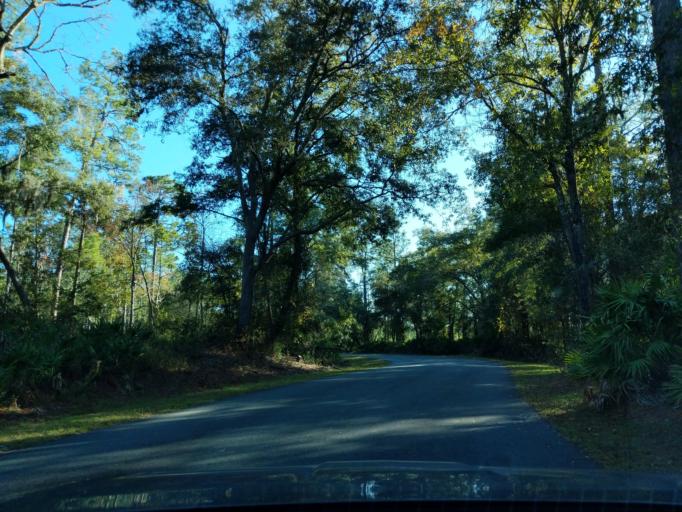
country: US
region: Georgia
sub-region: Charlton County
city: Folkston
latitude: 30.7387
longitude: -82.1370
